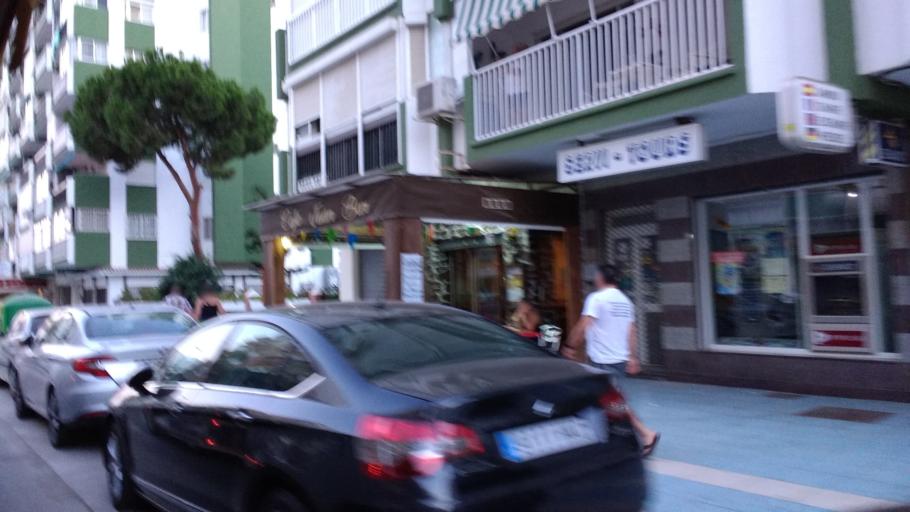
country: ES
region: Andalusia
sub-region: Provincia de Malaga
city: Velez-Malaga
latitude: 36.7370
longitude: -4.0979
